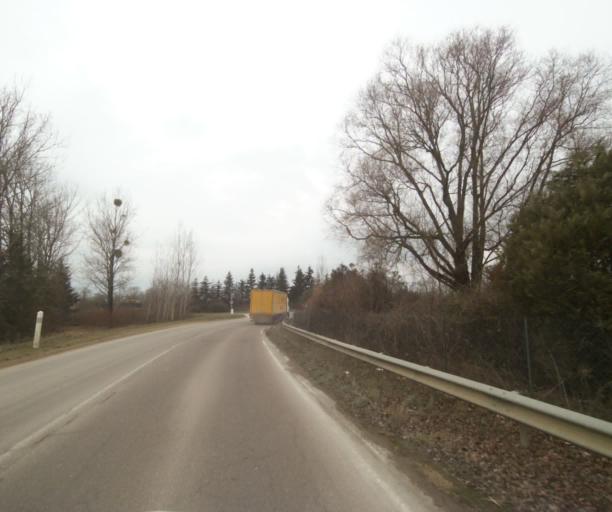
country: FR
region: Champagne-Ardenne
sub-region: Departement de la Haute-Marne
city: Villiers-en-Lieu
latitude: 48.6450
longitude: 4.9068
